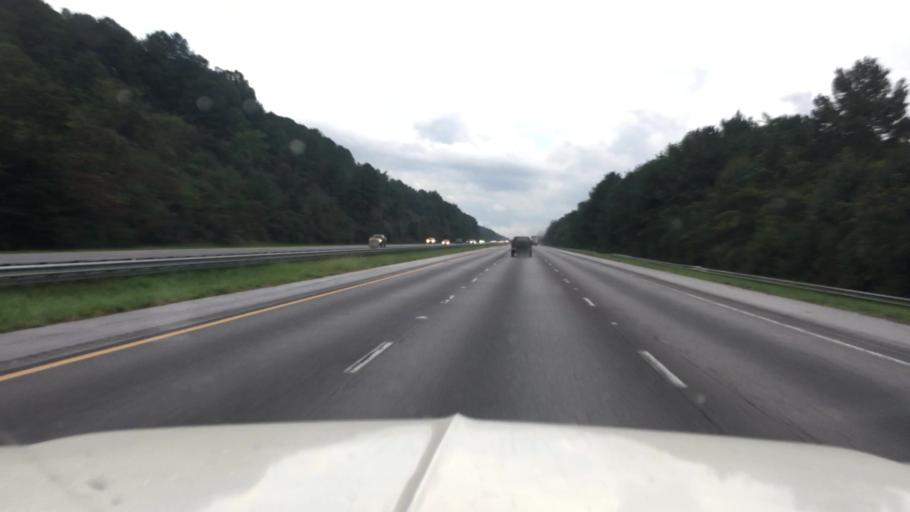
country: US
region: Alabama
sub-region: Jefferson County
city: Mount Olive
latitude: 33.6987
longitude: -86.8353
